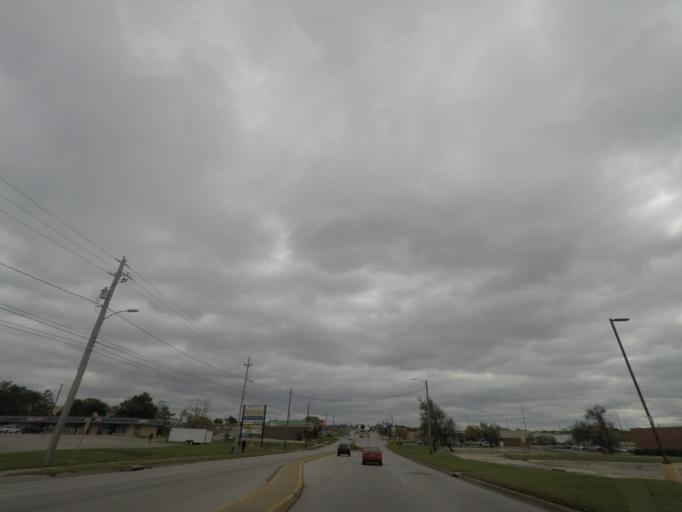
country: US
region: Iowa
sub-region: Polk County
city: Des Moines
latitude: 41.5263
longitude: -93.6033
